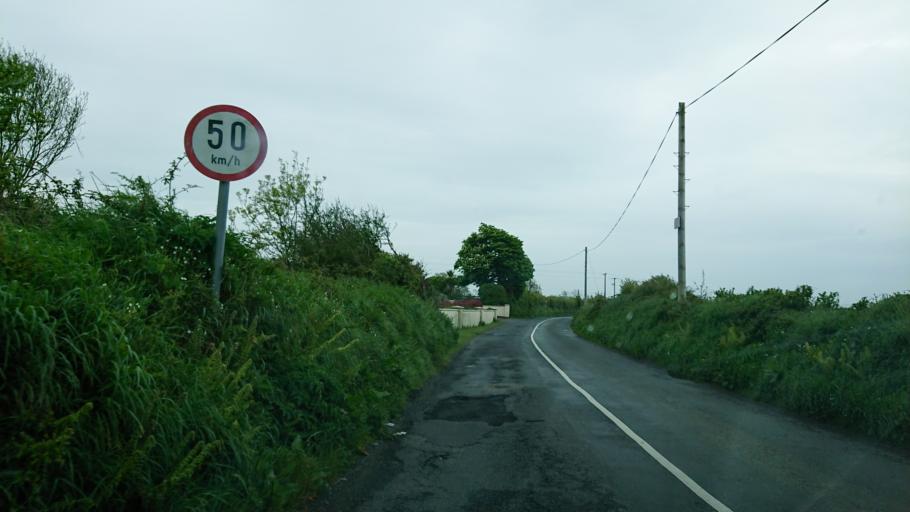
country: IE
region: Munster
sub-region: Waterford
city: Waterford
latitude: 52.2279
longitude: -7.0594
